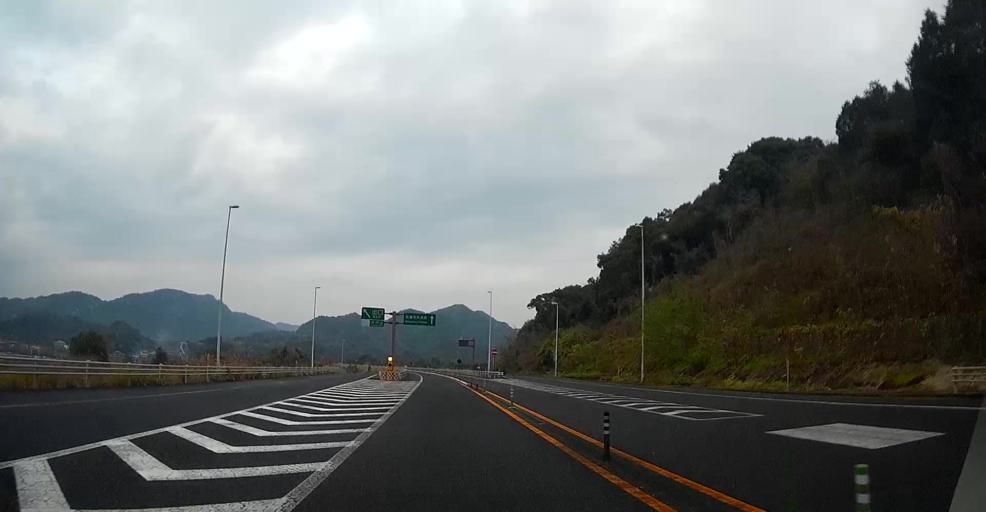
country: JP
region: Kumamoto
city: Hondo
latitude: 32.4969
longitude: 130.3885
